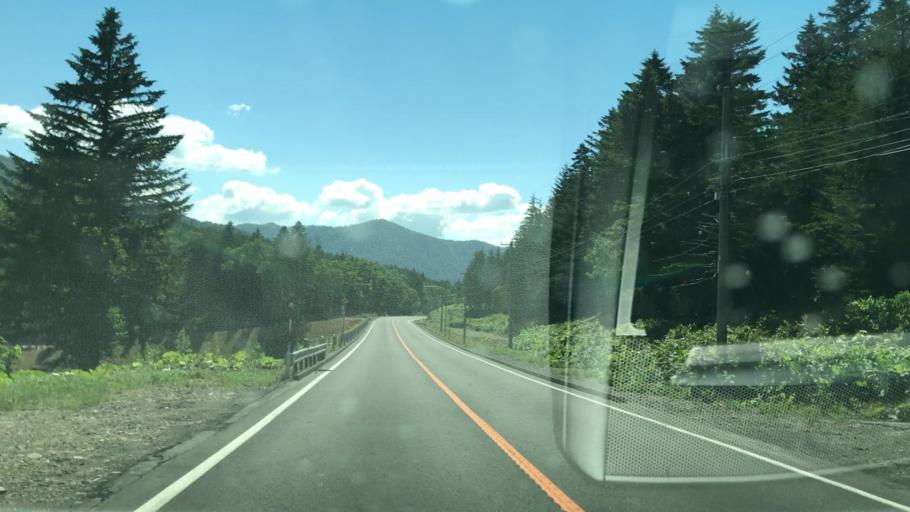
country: JP
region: Hokkaido
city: Shimo-furano
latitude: 42.9765
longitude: 142.6955
